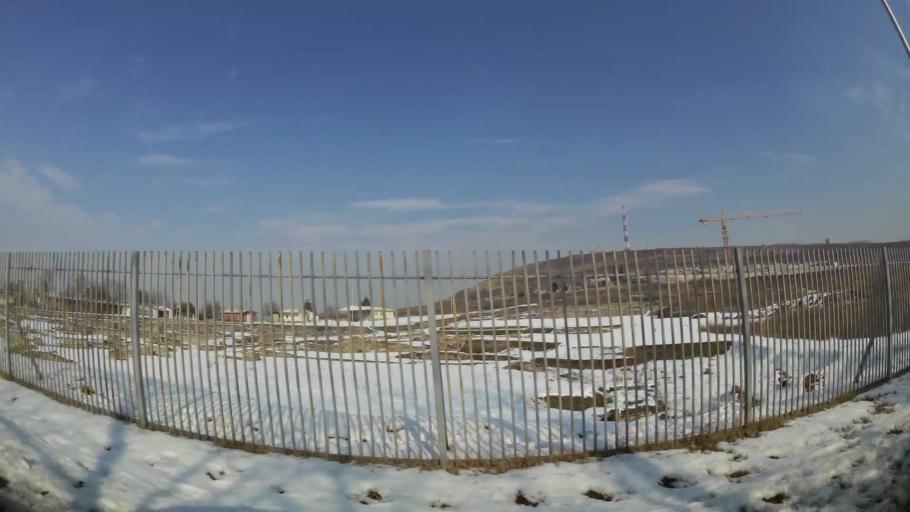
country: MK
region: Suto Orizari
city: Suto Orizare
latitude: 42.0161
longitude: 21.3916
